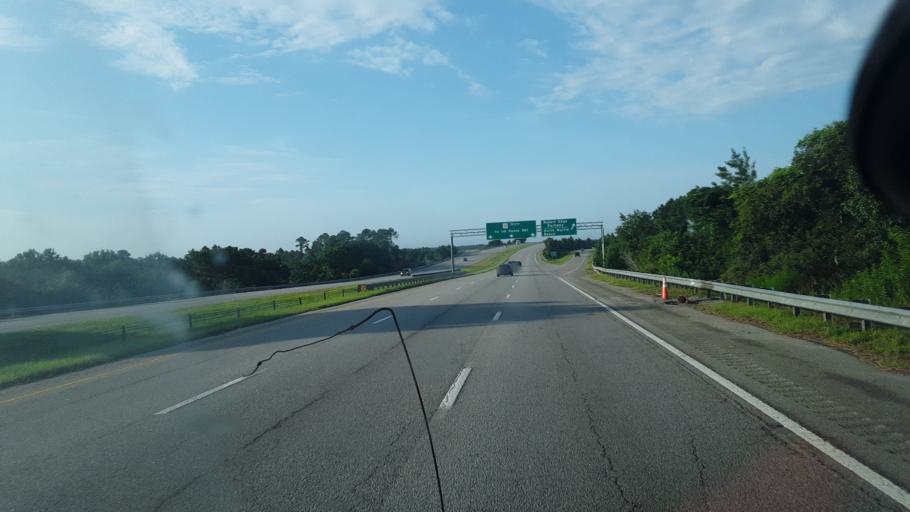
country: US
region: South Carolina
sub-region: Horry County
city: North Myrtle Beach
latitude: 33.8517
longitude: -78.6984
